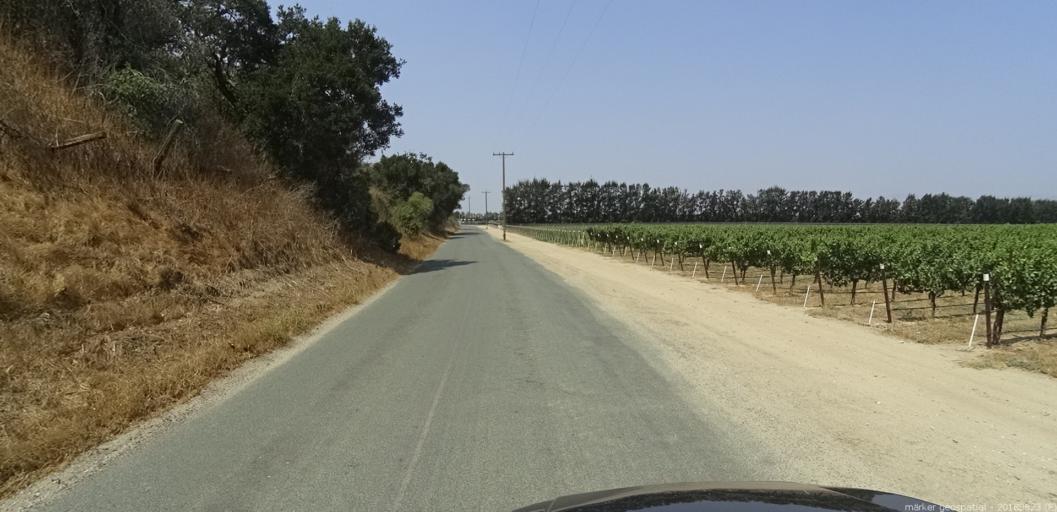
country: US
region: California
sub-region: Monterey County
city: Soledad
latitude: 36.3640
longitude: -121.3088
